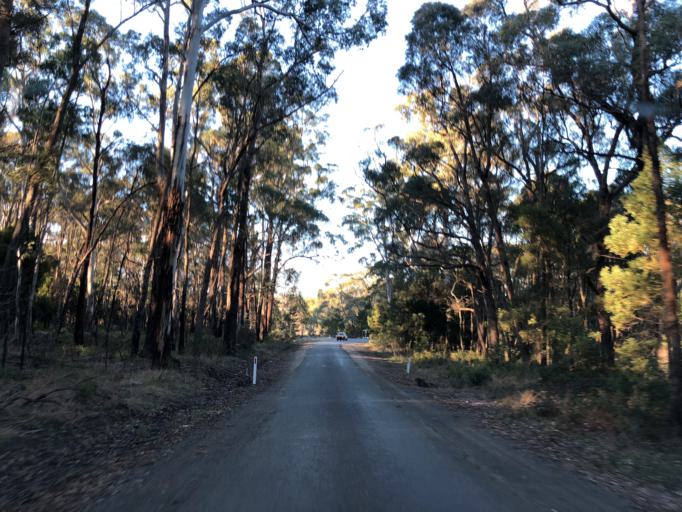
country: AU
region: Victoria
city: Brown Hill
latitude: -37.4814
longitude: 144.1494
